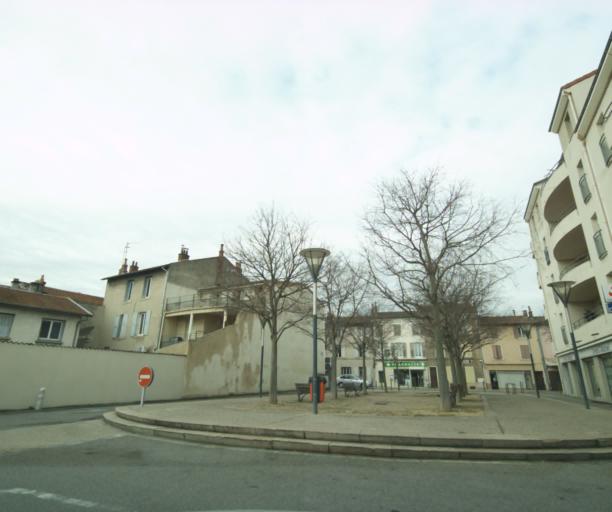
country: FR
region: Rhone-Alpes
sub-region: Departement de la Drome
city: Valence
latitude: 44.9443
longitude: 4.8948
